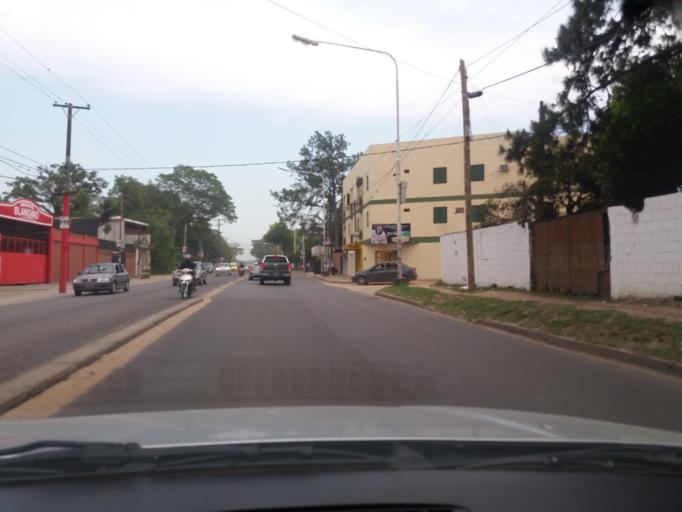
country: AR
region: Corrientes
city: Corrientes
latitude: -27.5035
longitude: -58.8122
